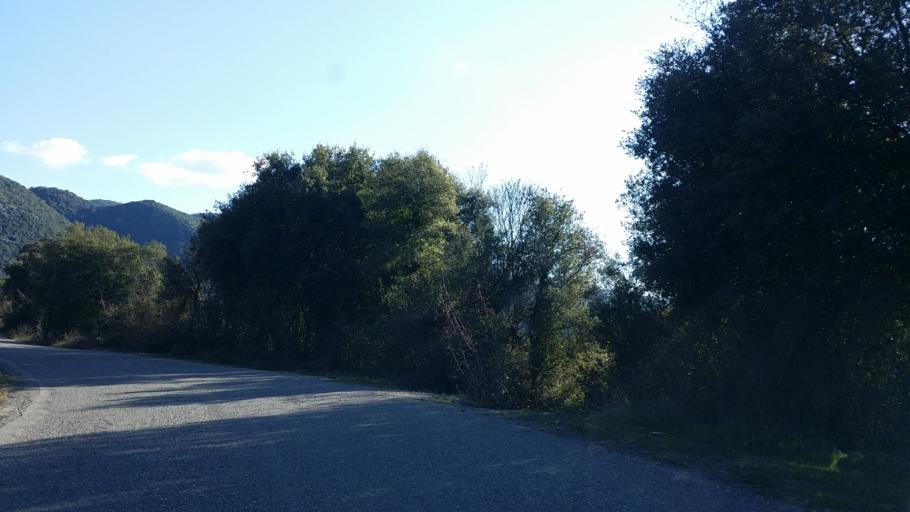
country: GR
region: Central Greece
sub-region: Nomos Evrytanias
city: Kerasochori
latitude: 38.9943
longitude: 21.5590
